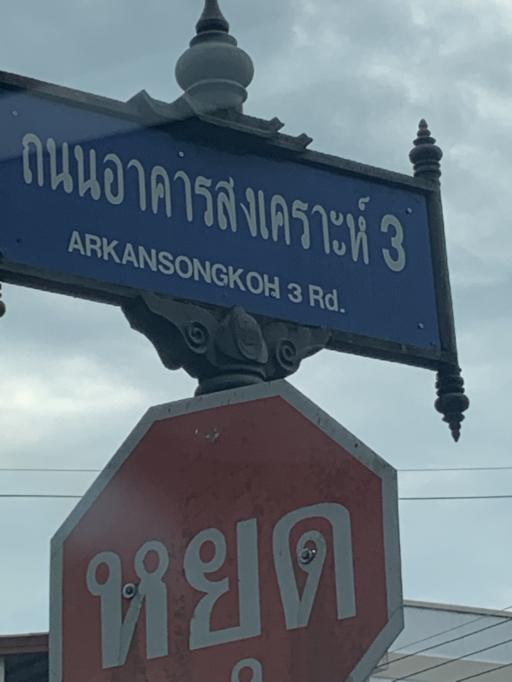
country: TH
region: Yala
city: Yala
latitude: 6.5452
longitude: 101.2925
